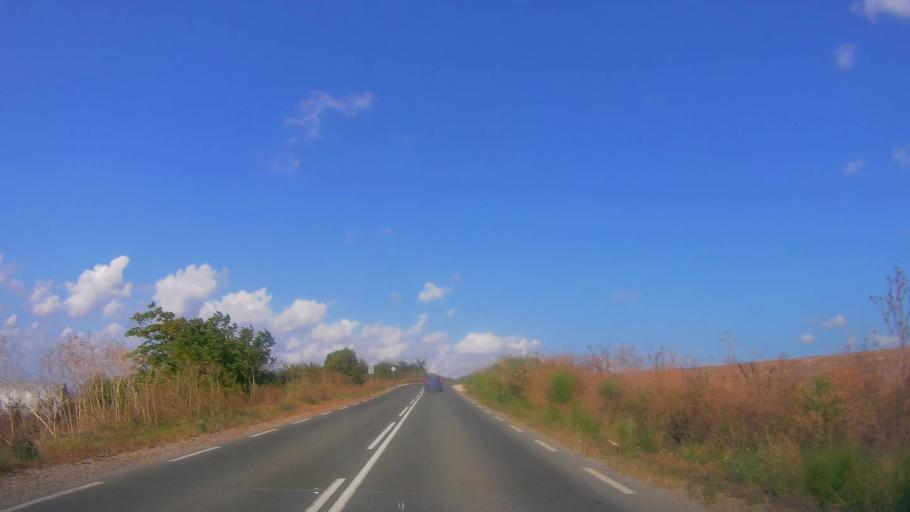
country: BG
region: Burgas
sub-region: Obshtina Burgas
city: Burgas
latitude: 42.4792
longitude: 27.3726
